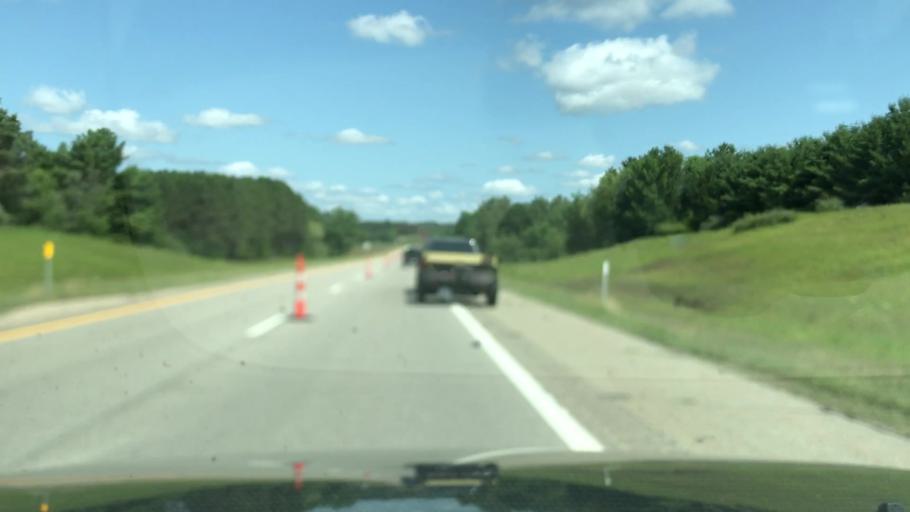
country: US
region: Michigan
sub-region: Mecosta County
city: Big Rapids
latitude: 43.7574
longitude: -85.5302
